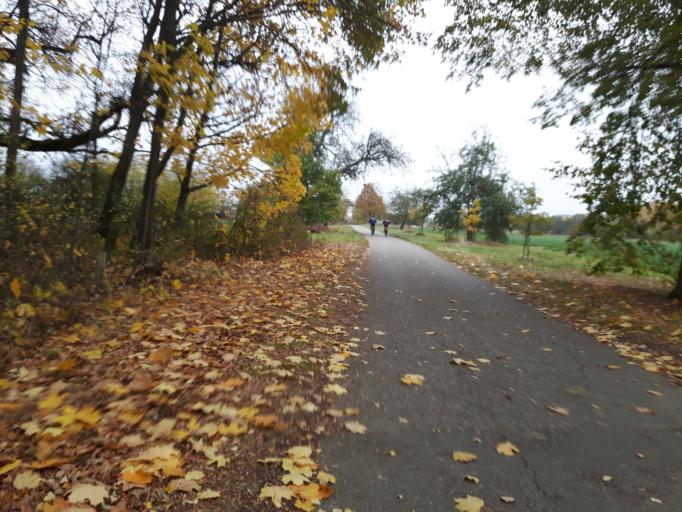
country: DE
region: Baden-Wuerttemberg
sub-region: Karlsruhe Region
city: Ostringen
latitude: 49.2179
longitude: 8.6845
